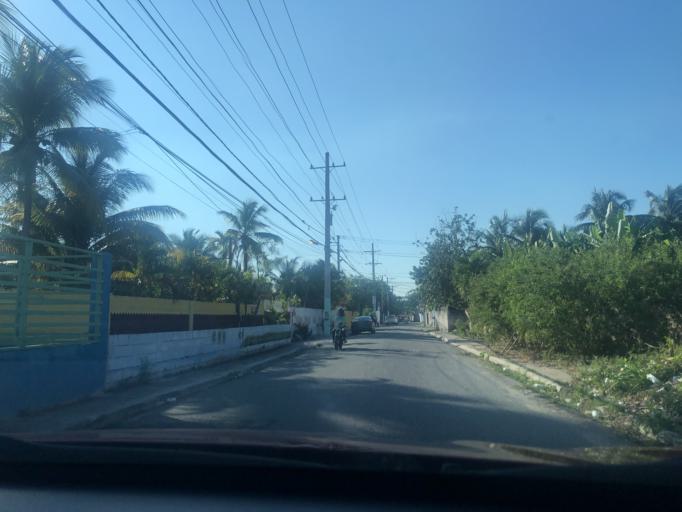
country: DO
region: Santo Domingo
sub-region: Santo Domingo
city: Boca Chica
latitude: 18.4536
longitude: -69.6090
